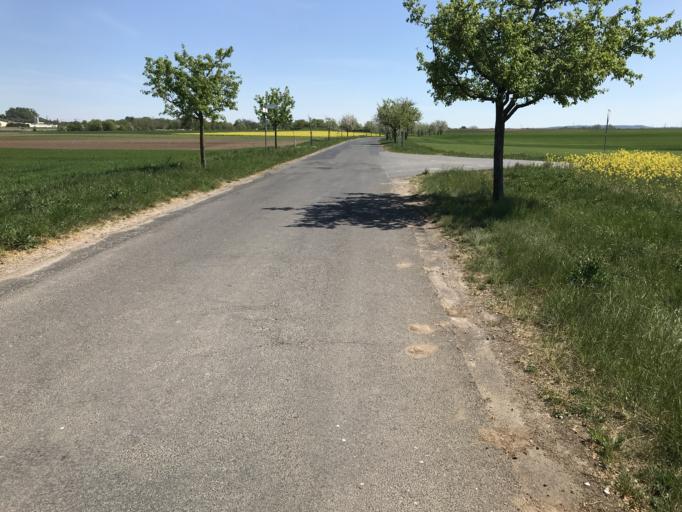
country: DE
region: Bavaria
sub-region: Regierungsbezirk Unterfranken
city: Iphofen
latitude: 49.6879
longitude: 10.2714
